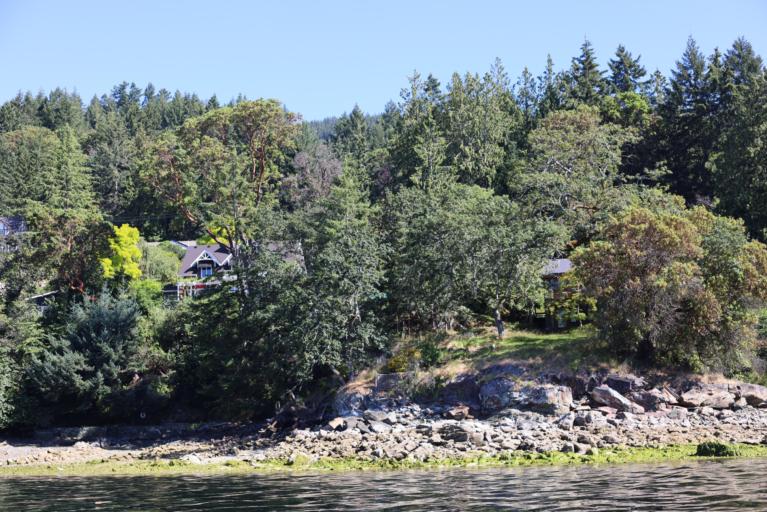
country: CA
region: British Columbia
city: North Cowichan
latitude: 48.8168
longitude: -123.6062
